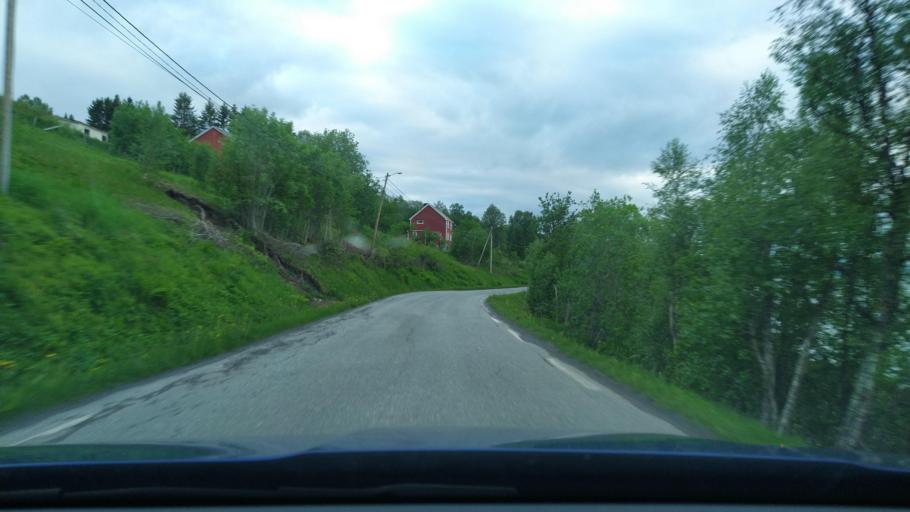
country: NO
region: Troms
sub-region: Tranoy
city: Vangsvika
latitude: 69.1309
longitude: 17.8725
